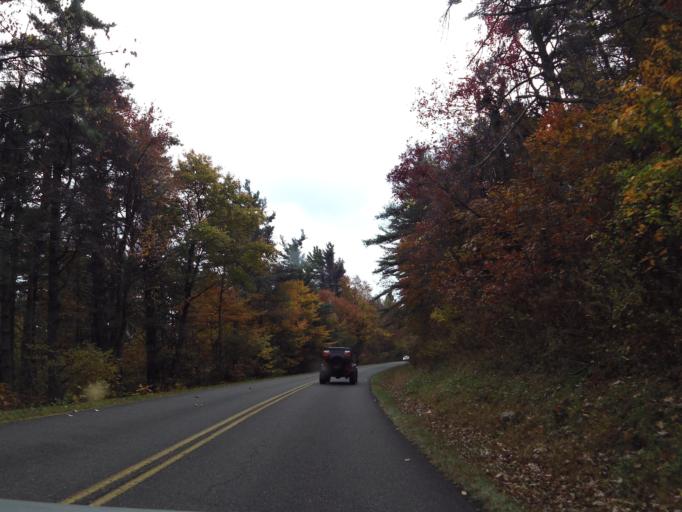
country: US
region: North Carolina
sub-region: Ashe County
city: West Jefferson
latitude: 36.2440
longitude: -81.4589
